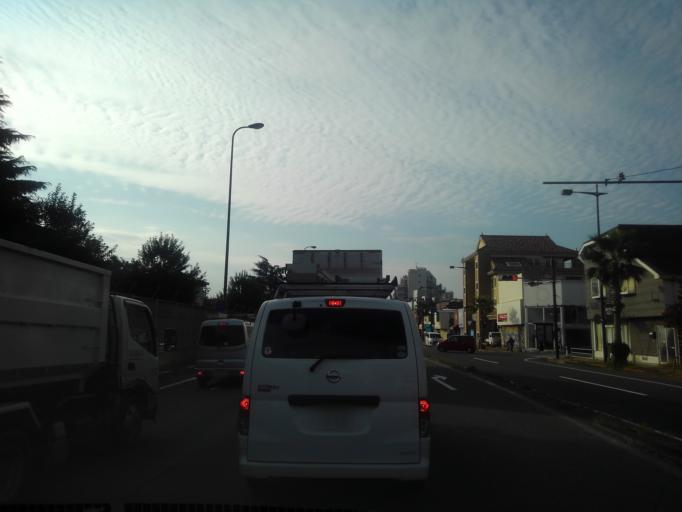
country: JP
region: Tokyo
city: Fussa
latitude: 35.7450
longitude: 139.3376
